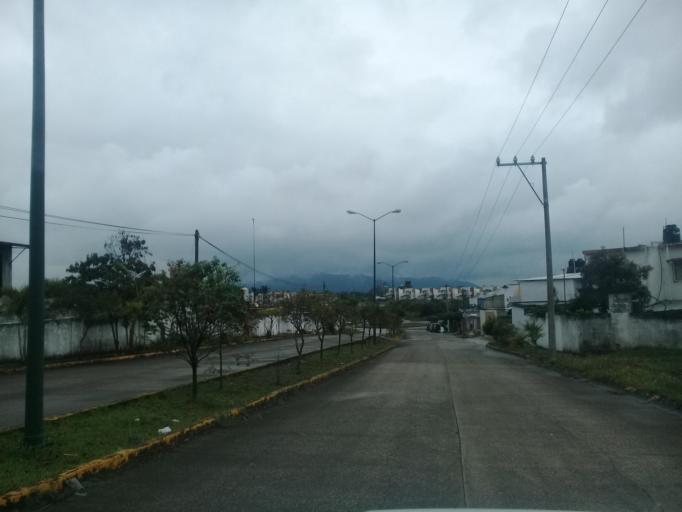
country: MX
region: Veracruz
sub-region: Cordoba
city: San Jose de Tapia
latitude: 18.8378
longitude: -96.9560
